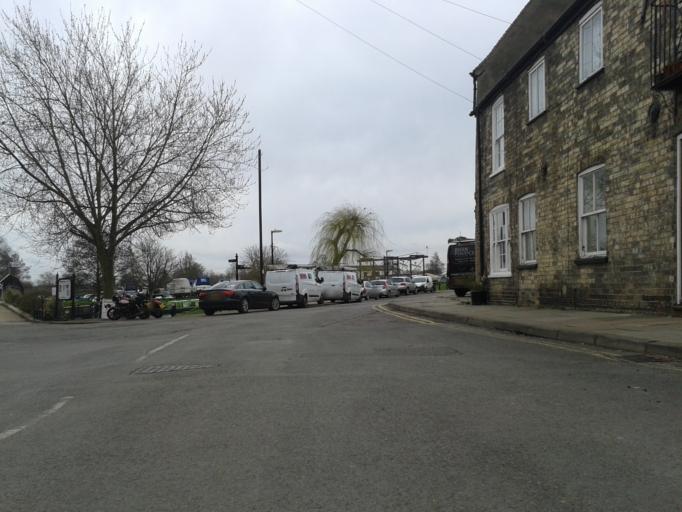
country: GB
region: England
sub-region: Cambridgeshire
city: Ely
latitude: 52.3962
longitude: 0.2701
